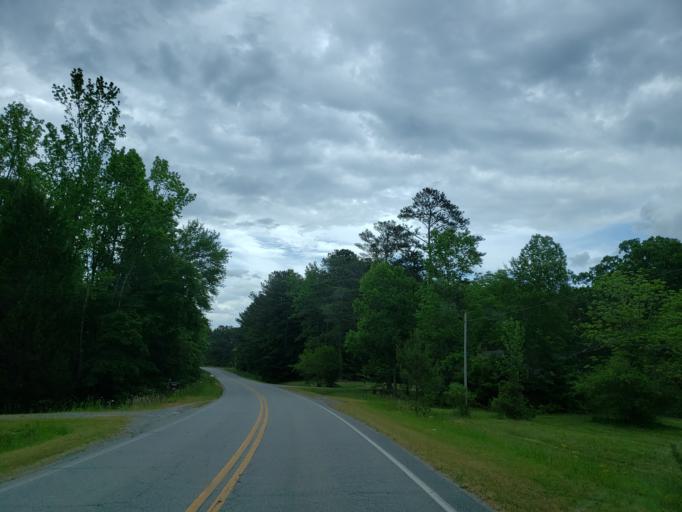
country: US
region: Georgia
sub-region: Polk County
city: Rockmart
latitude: 33.9268
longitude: -85.0581
